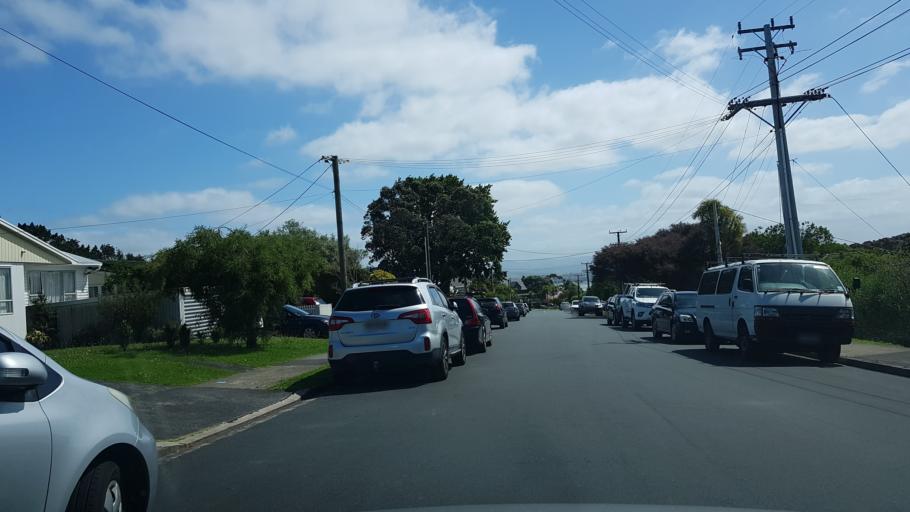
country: NZ
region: Auckland
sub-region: Auckland
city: North Shore
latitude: -36.8101
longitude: 174.6970
